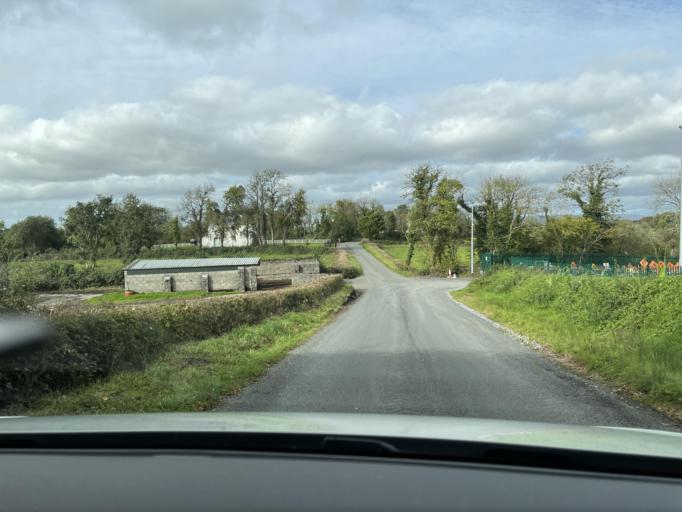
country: IE
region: Connaught
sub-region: County Leitrim
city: Carrick-on-Shannon
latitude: 53.9576
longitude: -8.0678
